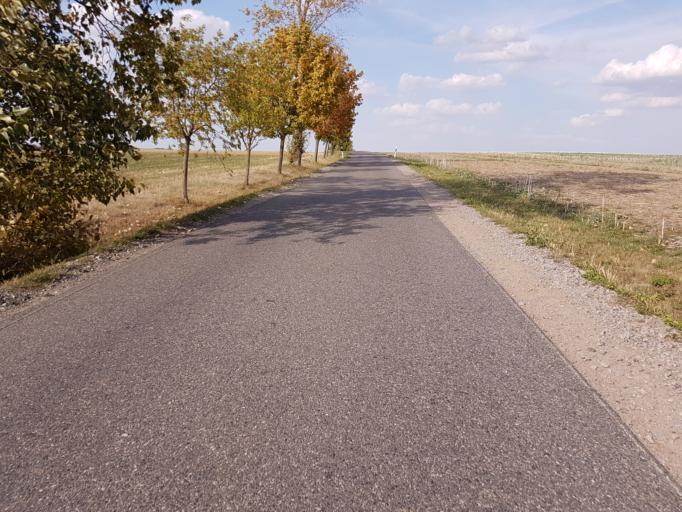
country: DE
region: Saxony
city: Claussnitz
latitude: 50.9613
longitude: 12.8824
